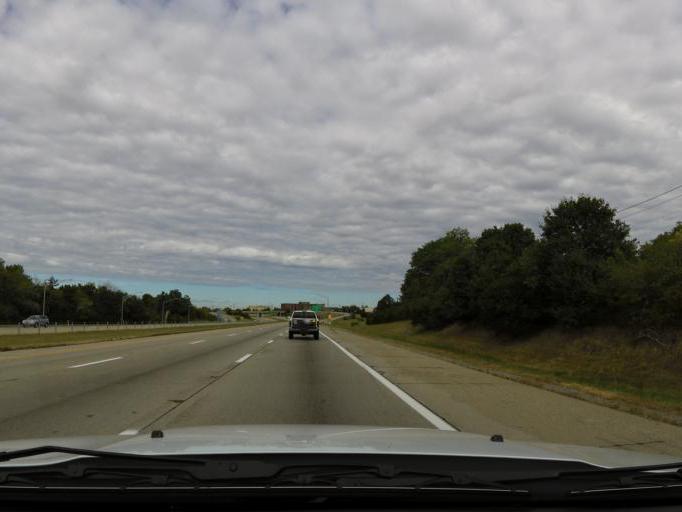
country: US
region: Kentucky
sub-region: Kenton County
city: Villa Hills
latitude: 39.0503
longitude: -84.6205
